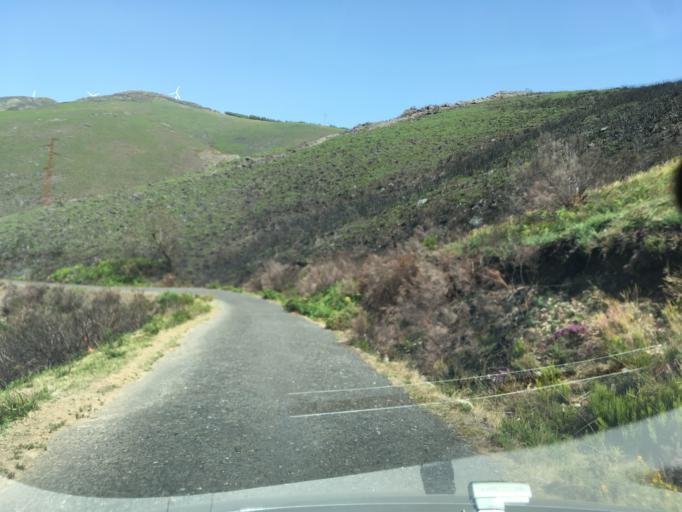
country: PT
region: Braga
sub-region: Celorico de Basto
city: Celorico de Basto
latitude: 41.2804
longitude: -7.9452
